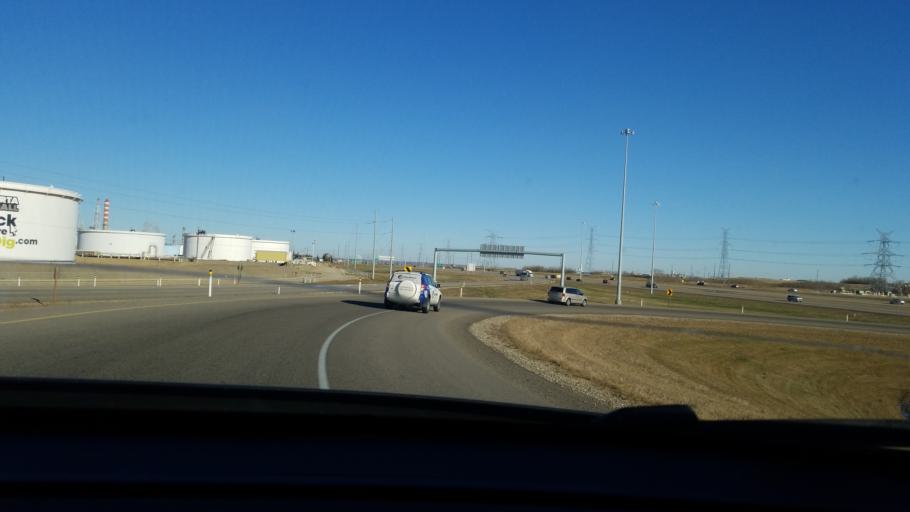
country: CA
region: Alberta
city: Sherwood Park
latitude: 53.5412
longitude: -113.3455
